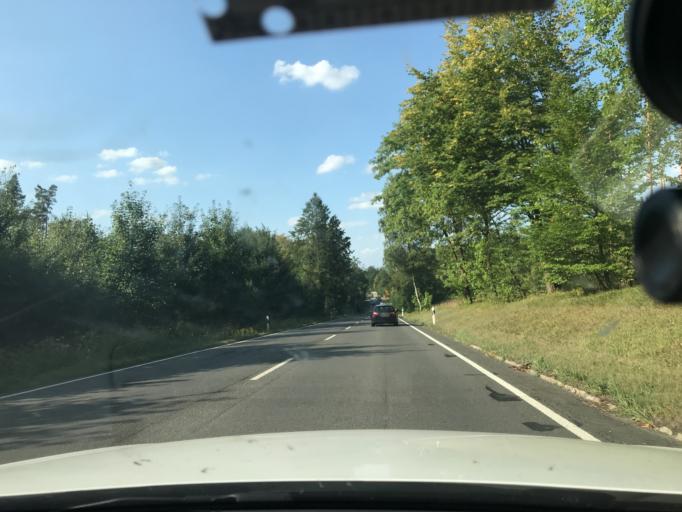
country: DE
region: Bavaria
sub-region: Upper Palatinate
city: Sulzbach-Rosenberg
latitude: 49.4903
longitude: 11.7319
